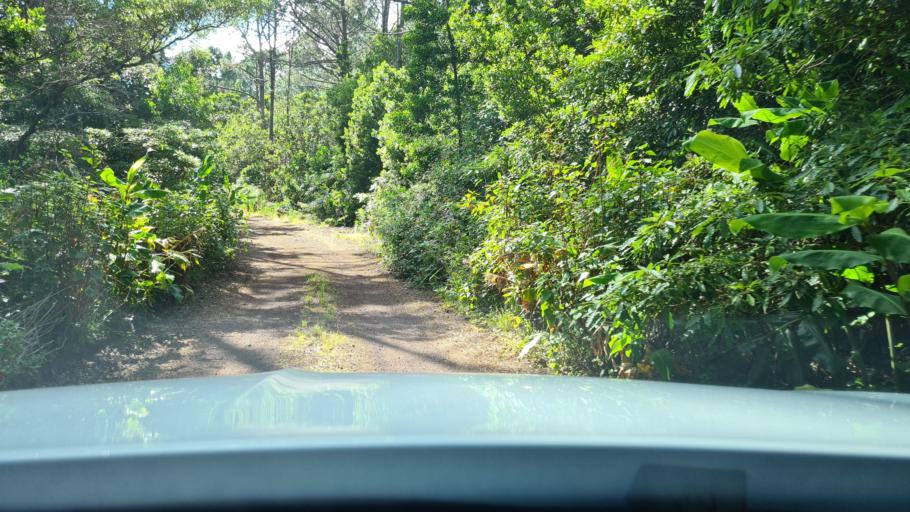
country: PT
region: Azores
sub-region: Sao Roque do Pico
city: Sao Roque do Pico
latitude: 38.4127
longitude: -28.3106
